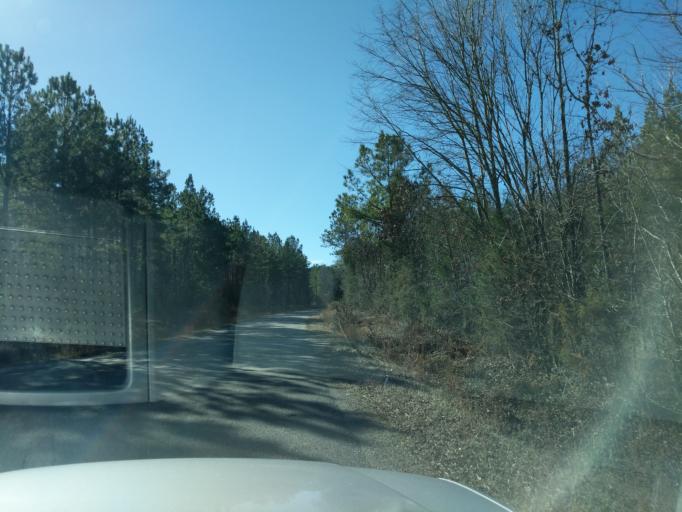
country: US
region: South Carolina
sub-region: Saluda County
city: Saluda
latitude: 34.0397
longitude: -81.8275
